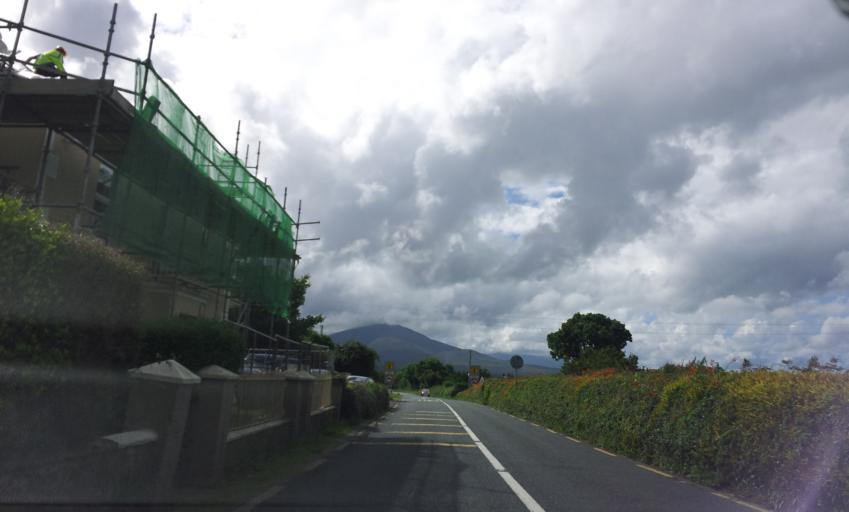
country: IE
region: Munster
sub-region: Ciarrai
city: Killorglin
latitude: 52.2260
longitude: -9.8943
